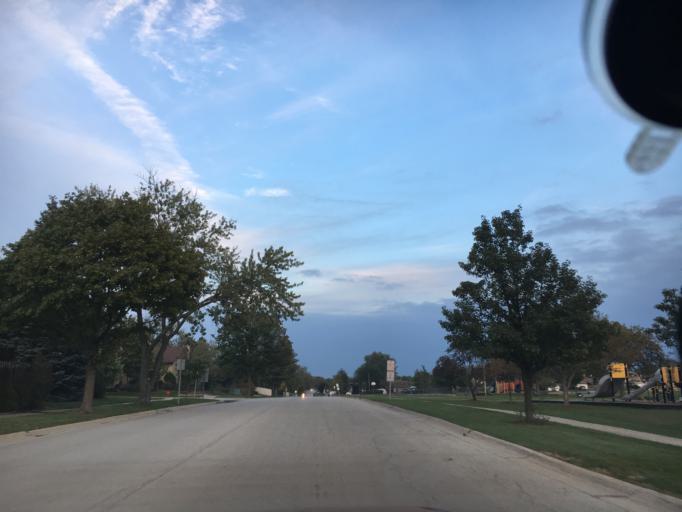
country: US
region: Illinois
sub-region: Cook County
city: Oak Forest
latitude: 41.6098
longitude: -87.7786
